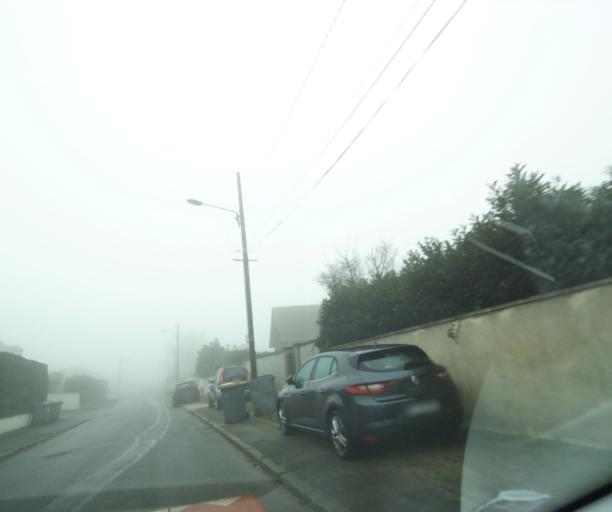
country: FR
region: Ile-de-France
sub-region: Departement de Seine-et-Marne
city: Dammartin-en-Goele
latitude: 49.0524
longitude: 2.6890
